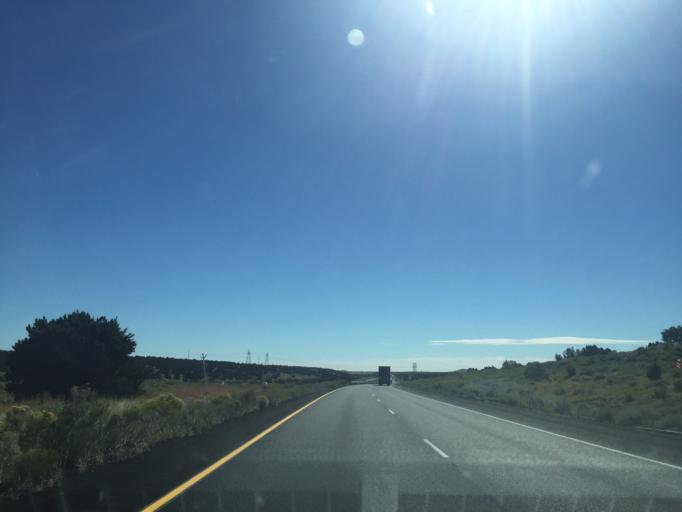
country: US
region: Arizona
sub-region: Coconino County
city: Flagstaff
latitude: 35.2015
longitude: -111.4068
